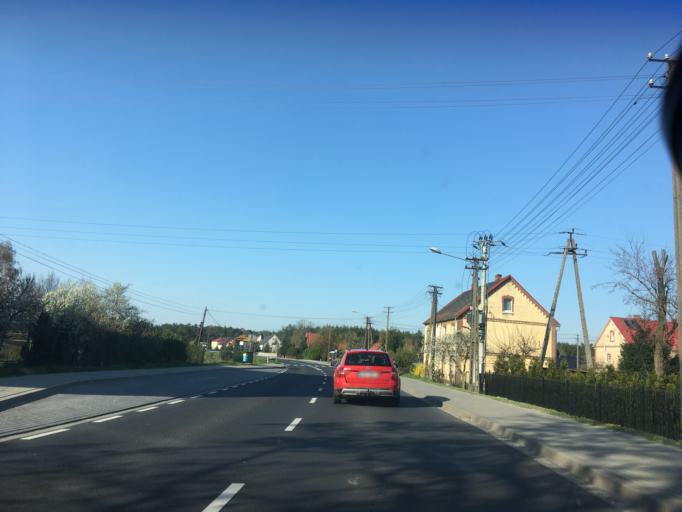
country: PL
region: Lubusz
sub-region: Powiat zaganski
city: Szprotawa
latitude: 51.4787
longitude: 15.6172
